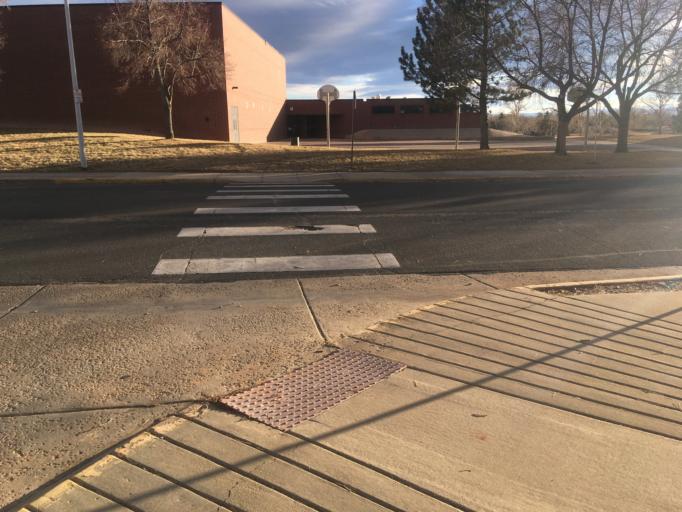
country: US
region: Colorado
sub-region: Broomfield County
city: Broomfield
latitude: 39.9387
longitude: -105.0791
